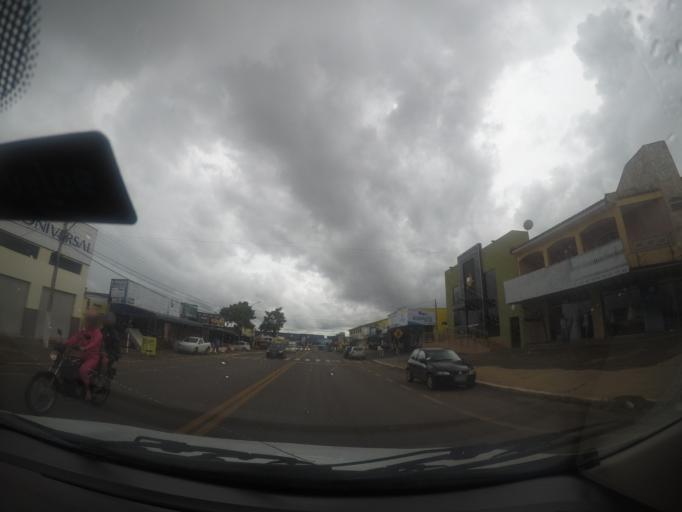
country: BR
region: Goias
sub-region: Trindade
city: Trindade
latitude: -16.6351
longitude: -49.3903
